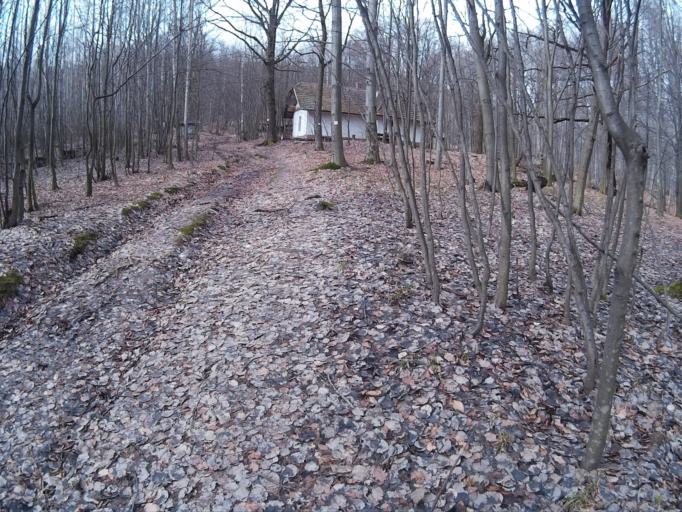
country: HU
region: Borsod-Abauj-Zemplen
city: Gonc
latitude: 48.4084
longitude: 21.4013
